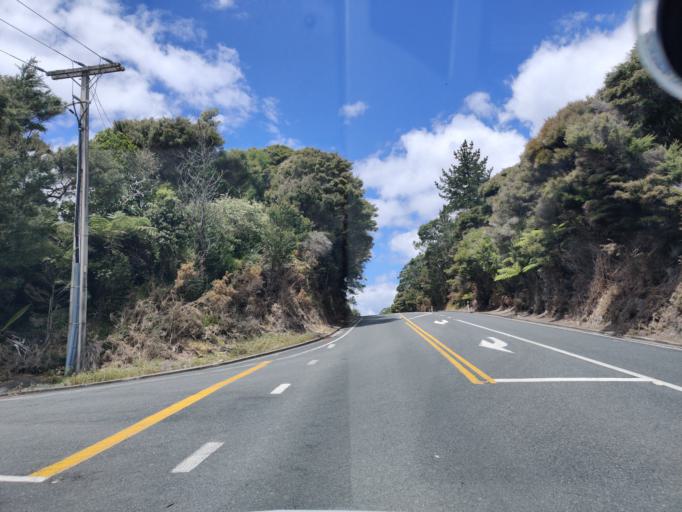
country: NZ
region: Northland
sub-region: Far North District
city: Paihia
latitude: -35.2674
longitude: 174.1327
